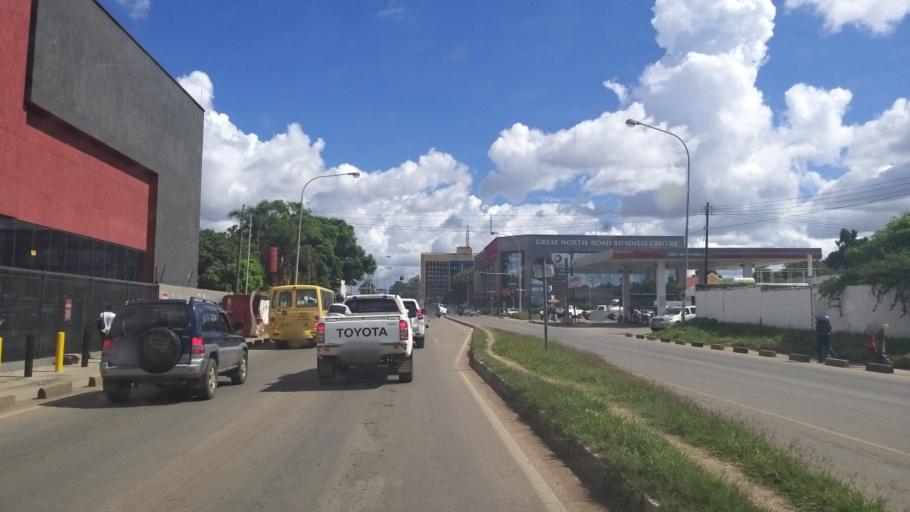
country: ZM
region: Lusaka
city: Lusaka
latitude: -15.4037
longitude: 28.2791
